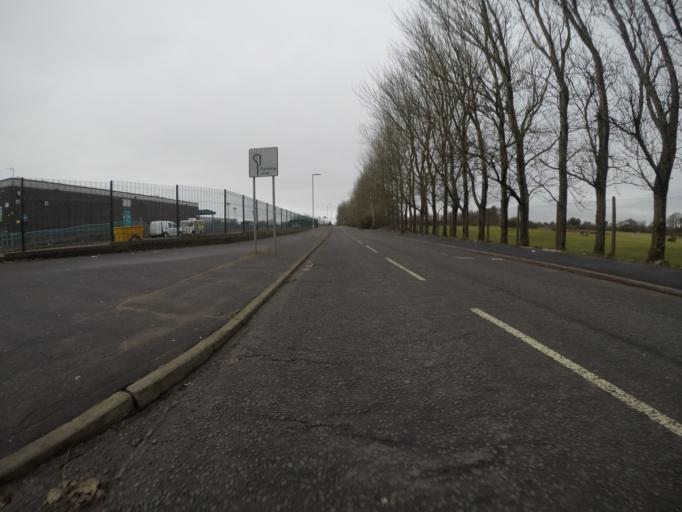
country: GB
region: Scotland
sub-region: North Ayrshire
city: Irvine
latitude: 55.6290
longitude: -4.6754
